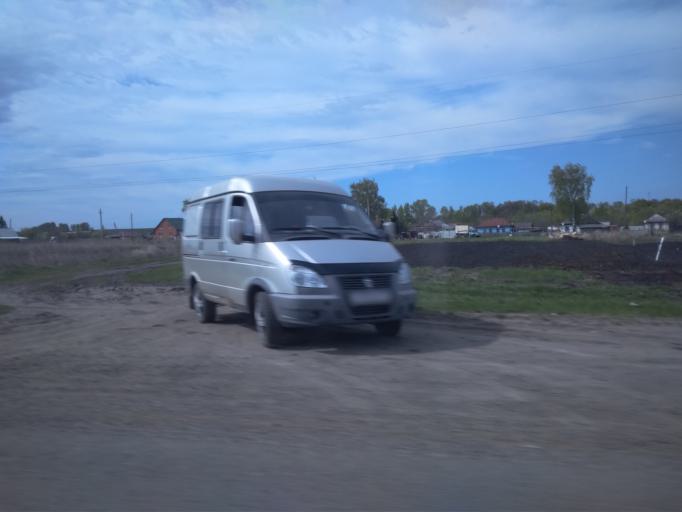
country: RU
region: Mordoviya
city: Atemar
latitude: 54.3175
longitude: 45.4721
